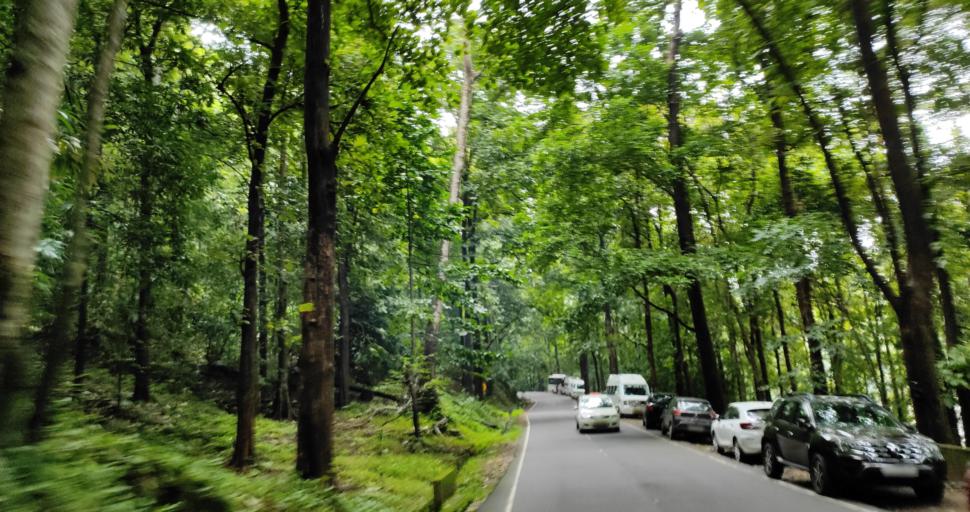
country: IN
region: Kerala
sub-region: Ernakulam
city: Angamali
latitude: 10.2901
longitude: 76.5677
